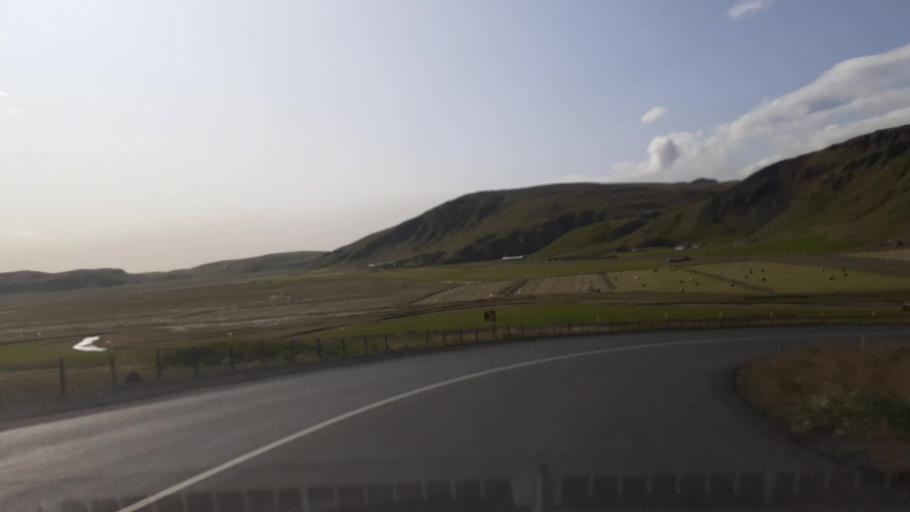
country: IS
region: South
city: Vestmannaeyjar
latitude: 63.4522
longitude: -19.0603
